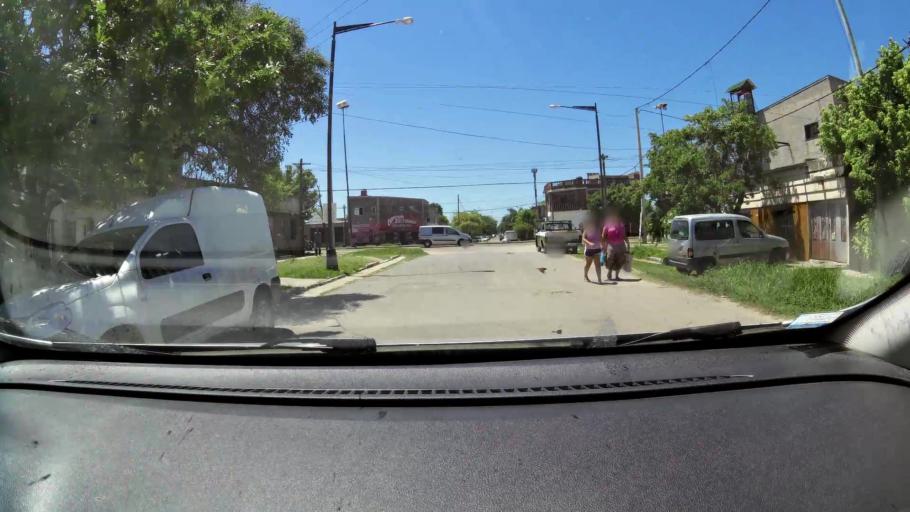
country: AR
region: Santa Fe
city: Santa Fe de la Vera Cruz
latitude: -31.6217
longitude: -60.7189
